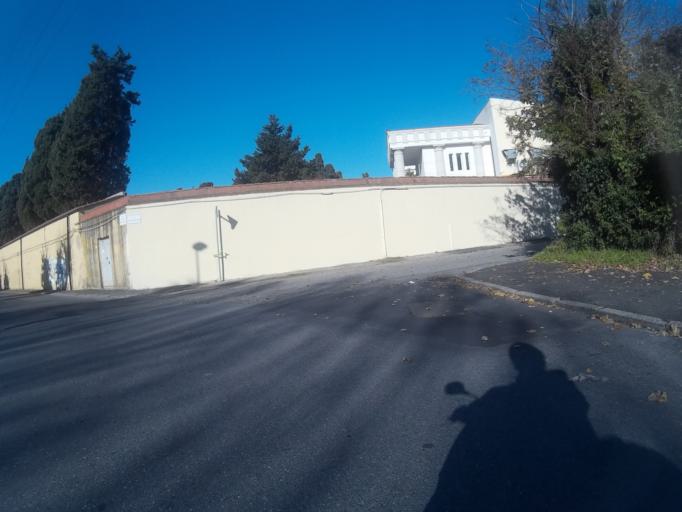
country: IT
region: Tuscany
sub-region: Provincia di Livorno
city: Livorno
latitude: 43.5678
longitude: 10.3270
